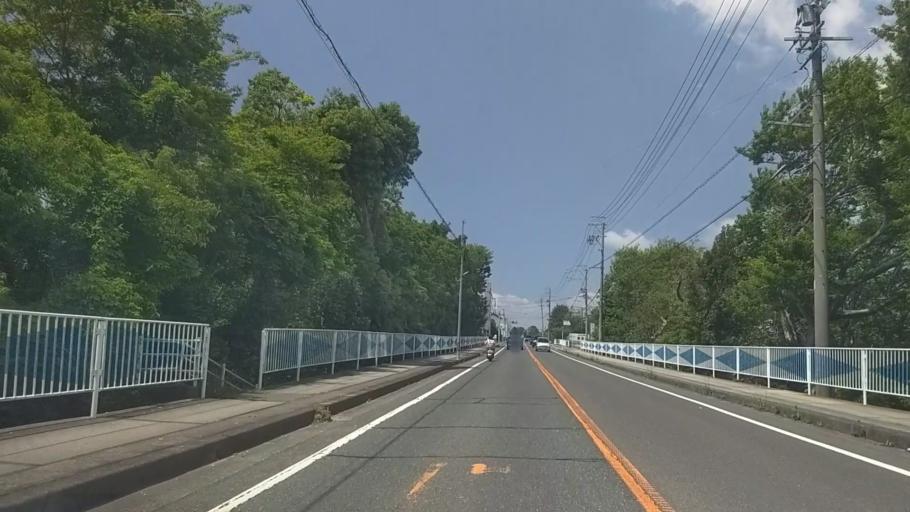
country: JP
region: Shizuoka
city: Hamamatsu
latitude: 34.7404
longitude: 137.7016
